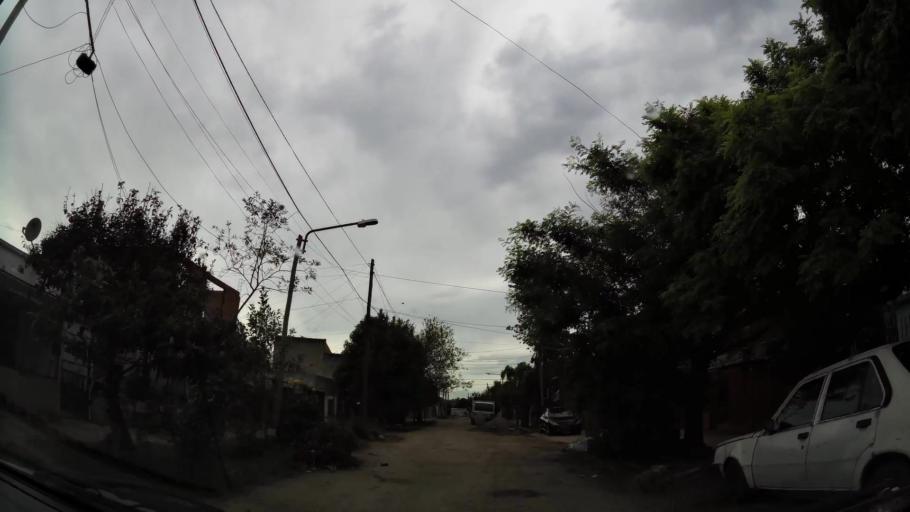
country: AR
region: Buenos Aires
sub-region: Partido de Quilmes
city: Quilmes
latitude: -34.7919
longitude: -58.2650
